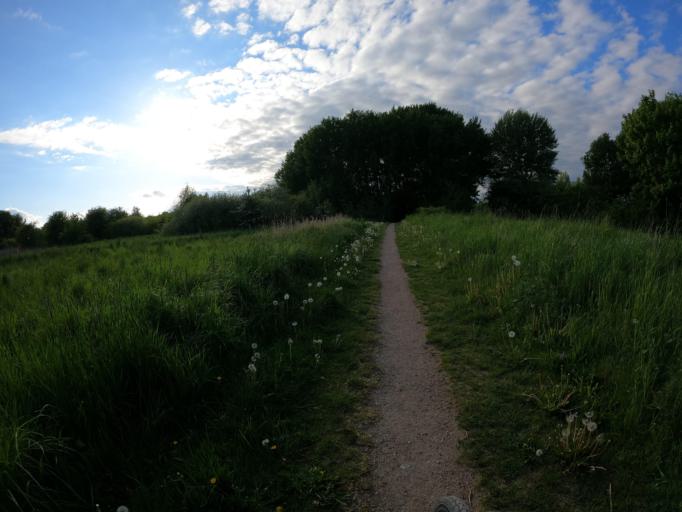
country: DK
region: Capital Region
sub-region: Ishoj Kommune
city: Ishoj
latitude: 55.6074
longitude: 12.3376
